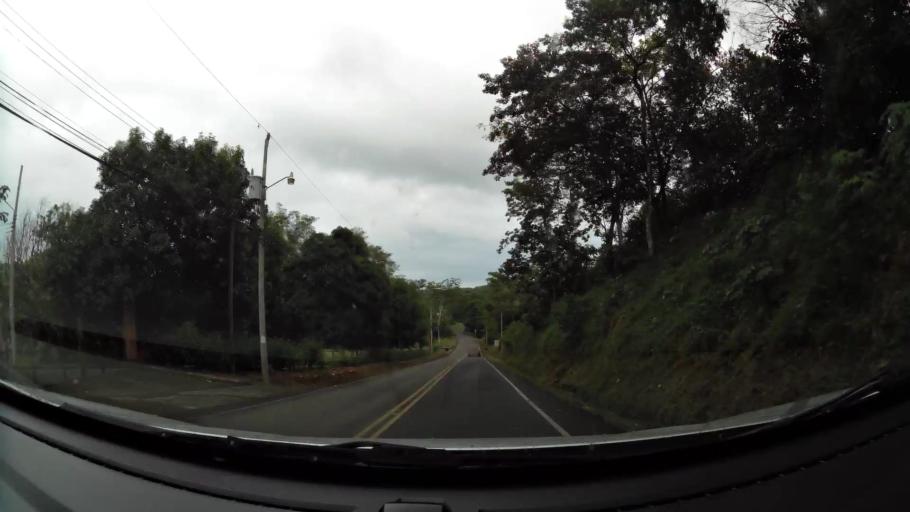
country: CR
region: Puntarenas
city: Esparza
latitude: 9.9849
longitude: -84.6264
